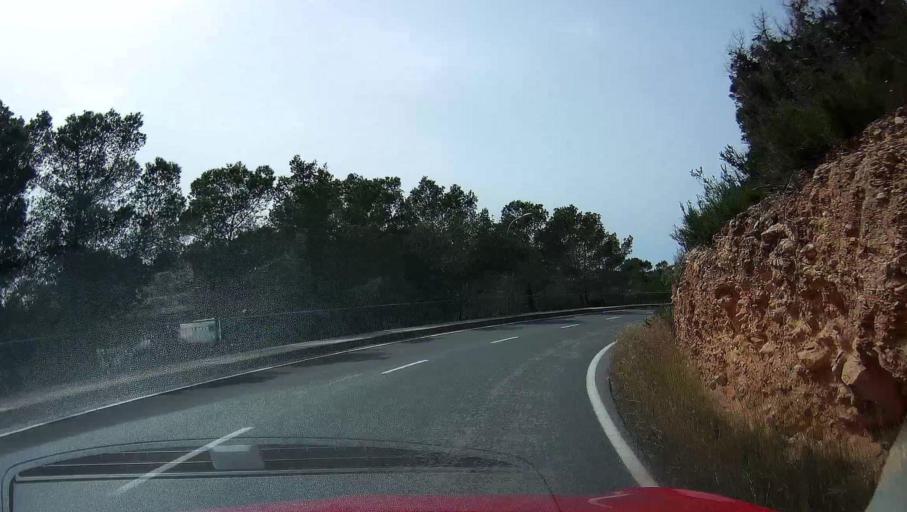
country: ES
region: Balearic Islands
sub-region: Illes Balears
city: Sant Joan de Labritja
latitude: 39.1079
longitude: 1.5207
